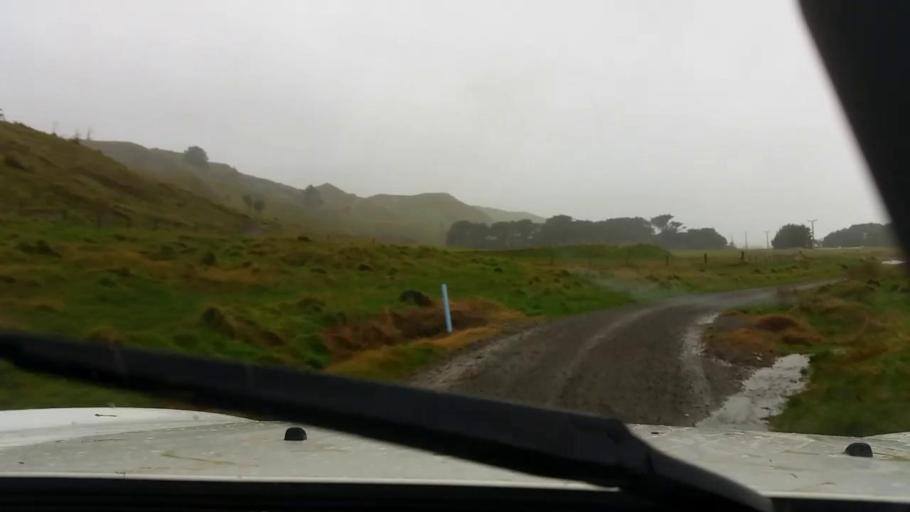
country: NZ
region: Wellington
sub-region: Masterton District
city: Masterton
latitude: -41.2597
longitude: 175.8980
